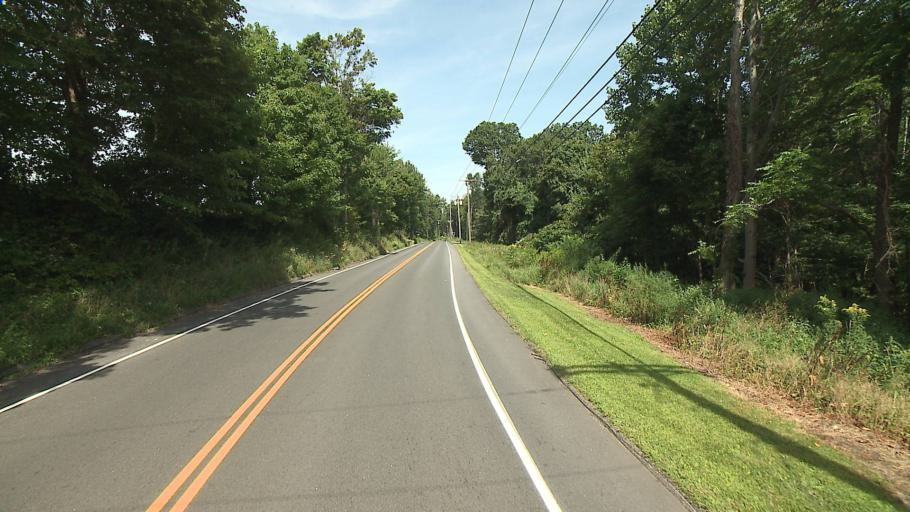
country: US
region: Connecticut
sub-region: Litchfield County
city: Bethlehem Village
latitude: 41.6160
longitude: -73.1966
